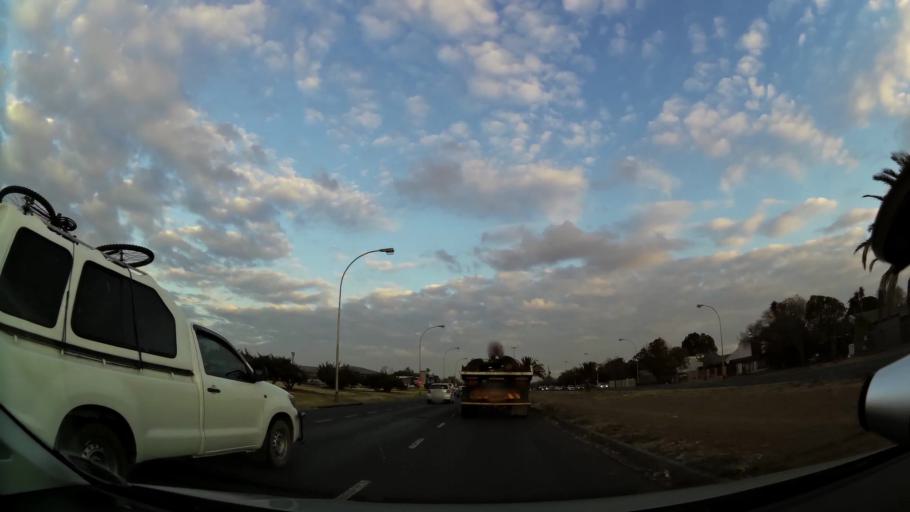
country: ZA
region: Orange Free State
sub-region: Mangaung Metropolitan Municipality
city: Bloemfontein
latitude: -29.1585
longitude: 26.1893
